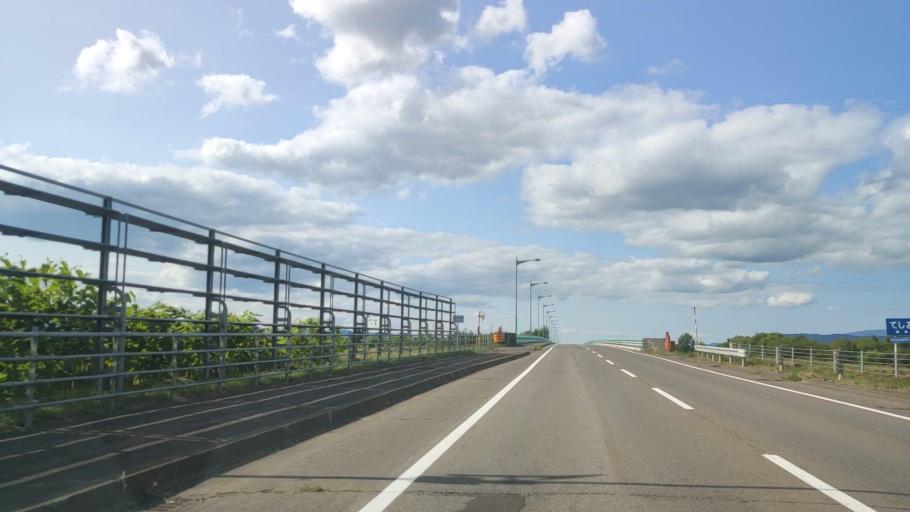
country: JP
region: Hokkaido
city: Nayoro
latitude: 44.4529
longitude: 142.3602
